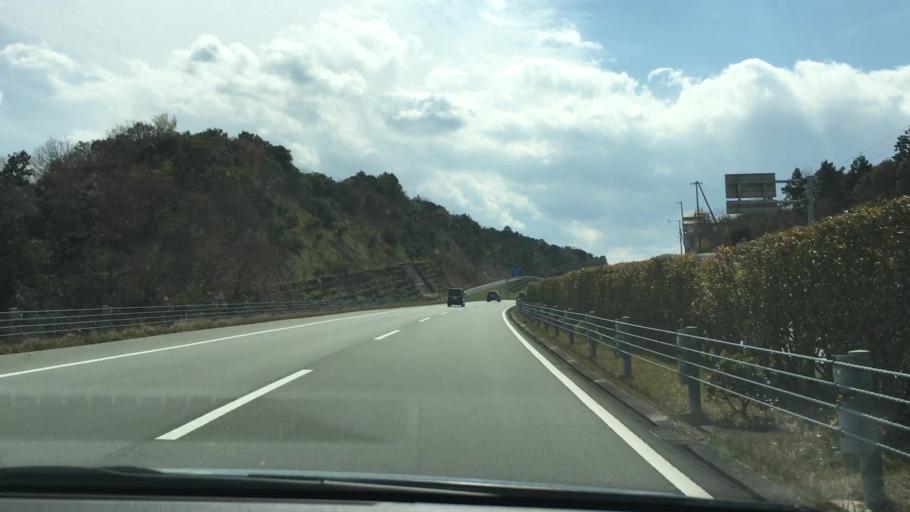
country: JP
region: Mie
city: Ise
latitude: 34.4820
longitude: 136.7514
